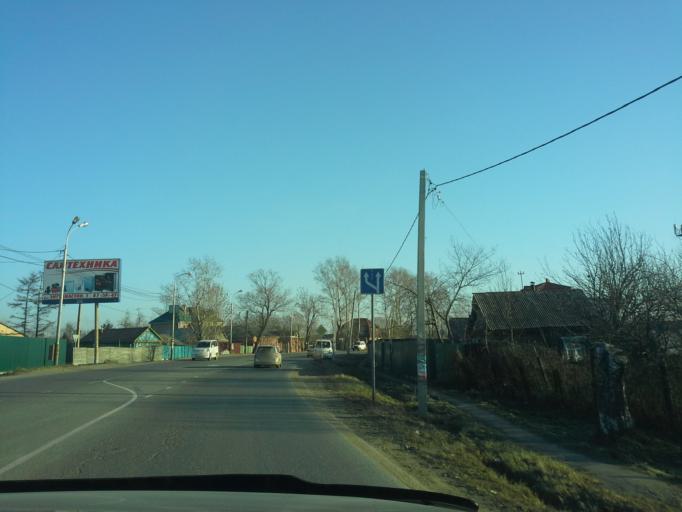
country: RU
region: Khabarovsk Krai
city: Topolevo
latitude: 48.4726
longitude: 135.1757
